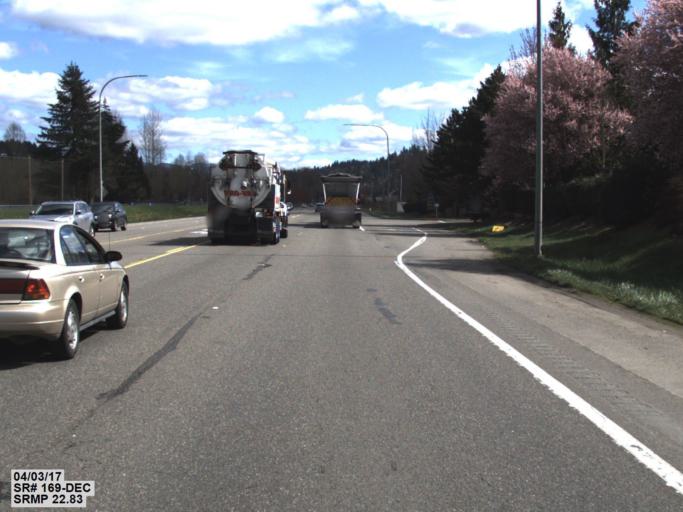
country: US
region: Washington
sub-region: King County
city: Fairwood
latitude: 47.4678
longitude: -122.1532
